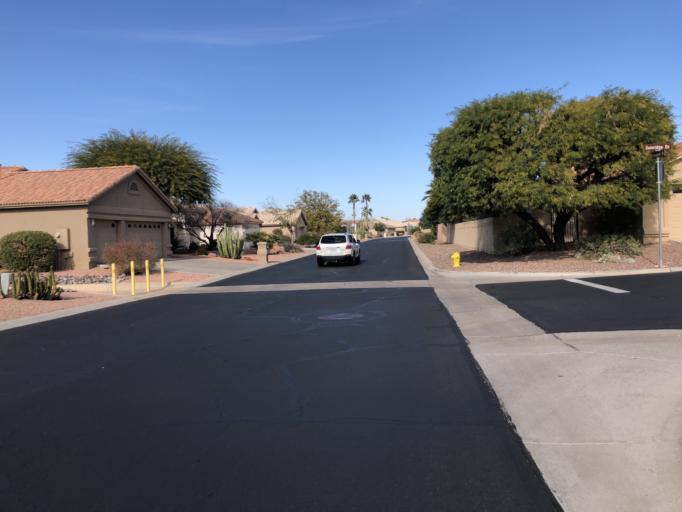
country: US
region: Arizona
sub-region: Maricopa County
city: Sun Lakes
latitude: 33.2283
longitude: -111.8705
